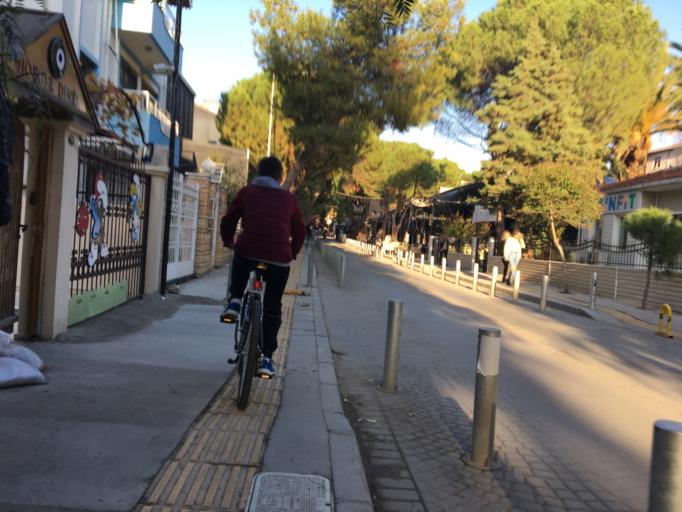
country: TR
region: Izmir
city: Buca
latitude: 38.3877
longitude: 27.1645
